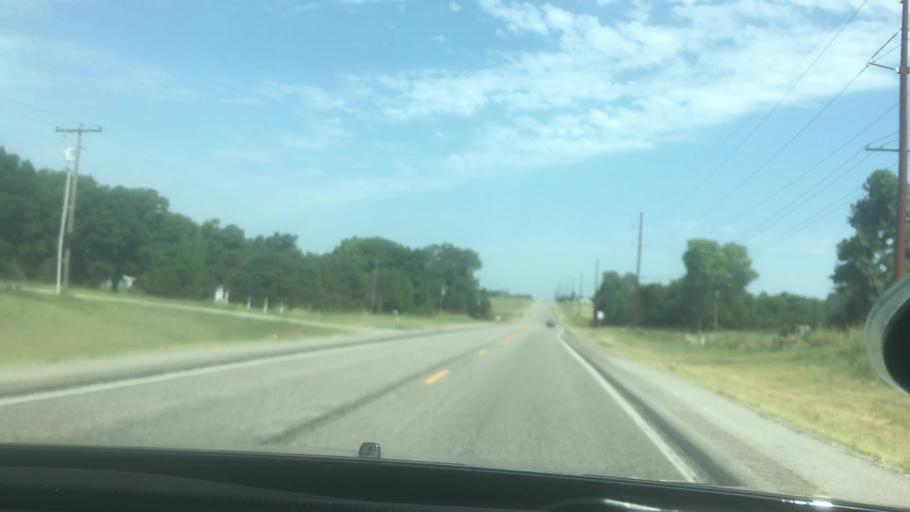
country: US
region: Oklahoma
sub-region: Seminole County
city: Konawa
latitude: 34.8447
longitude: -96.8024
